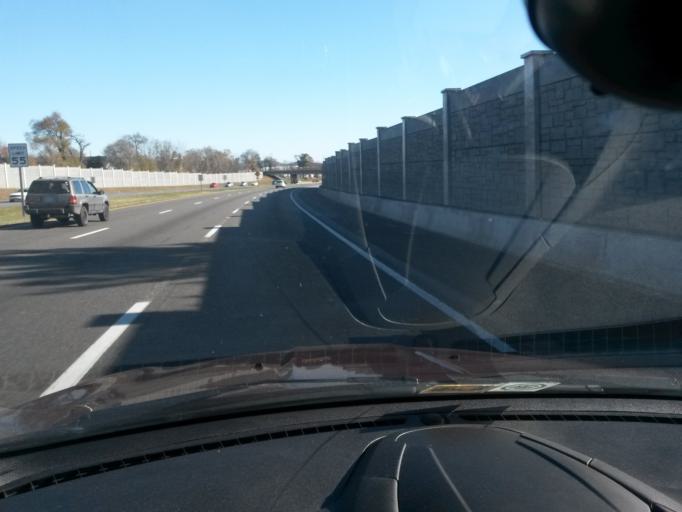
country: US
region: Virginia
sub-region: City of Roanoke
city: Roanoke
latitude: 37.2920
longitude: -79.9443
